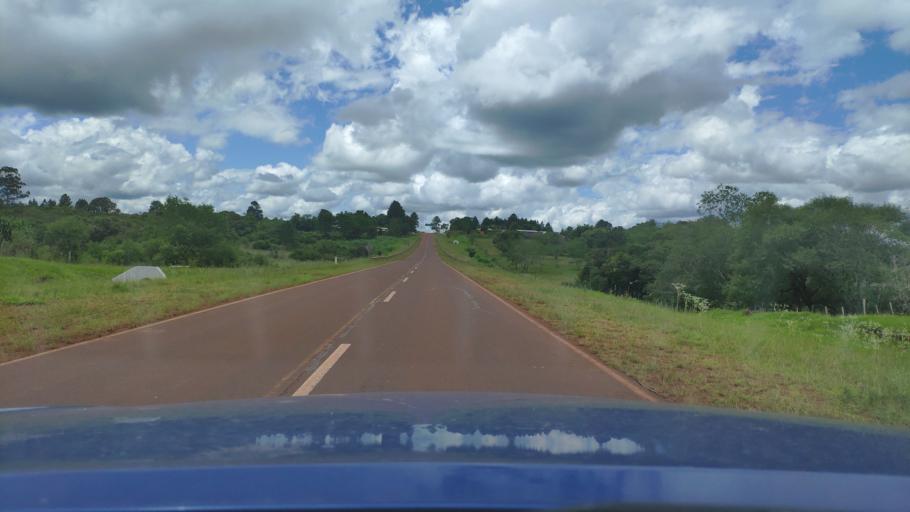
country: AR
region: Misiones
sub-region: Departamento de San Javier
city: San Javier
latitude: -27.8398
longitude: -55.2282
